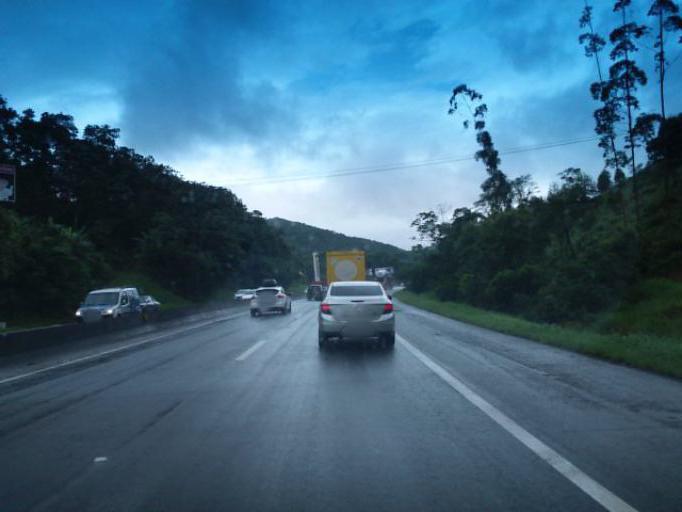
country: BR
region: Santa Catarina
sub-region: Balneario Camboriu
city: Balneario Camboriu
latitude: -26.9672
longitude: -48.6837
